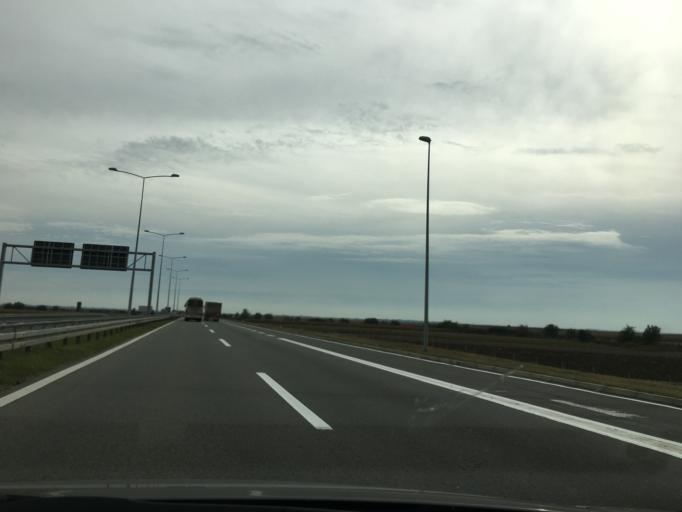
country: RS
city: Novi Karlovci
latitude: 45.0686
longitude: 20.1533
